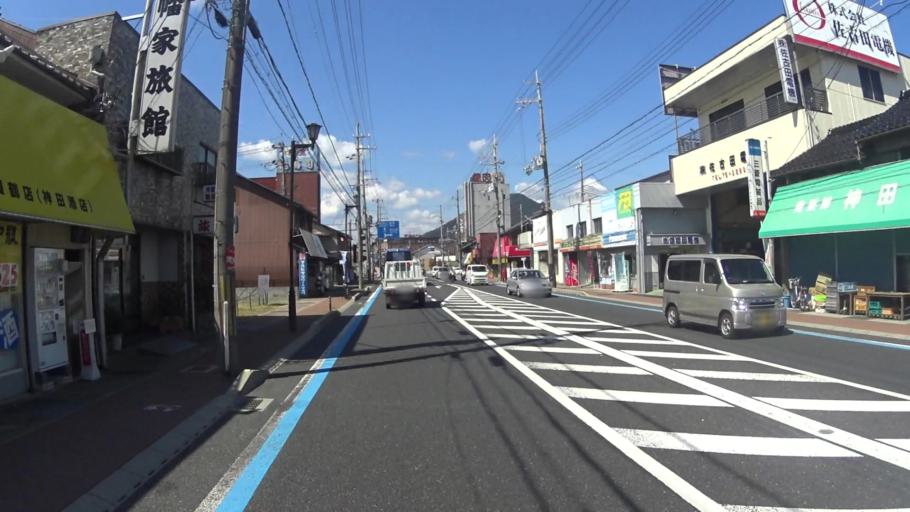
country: JP
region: Kyoto
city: Maizuru
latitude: 35.4510
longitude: 135.3248
